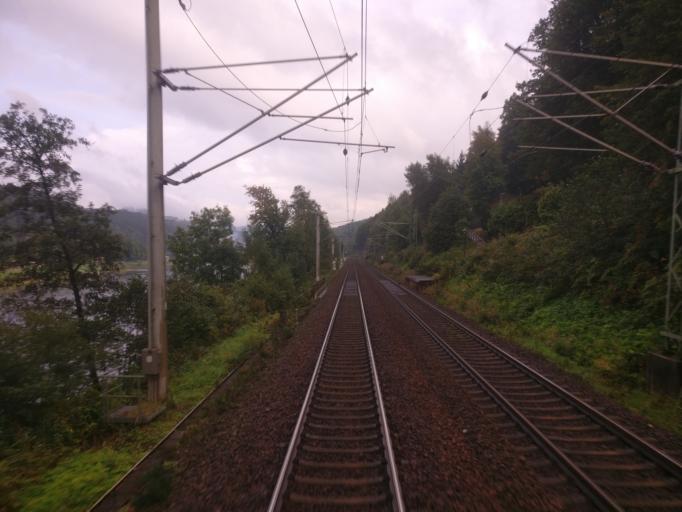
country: DE
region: Saxony
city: Bad Schandau
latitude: 50.9156
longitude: 14.1508
